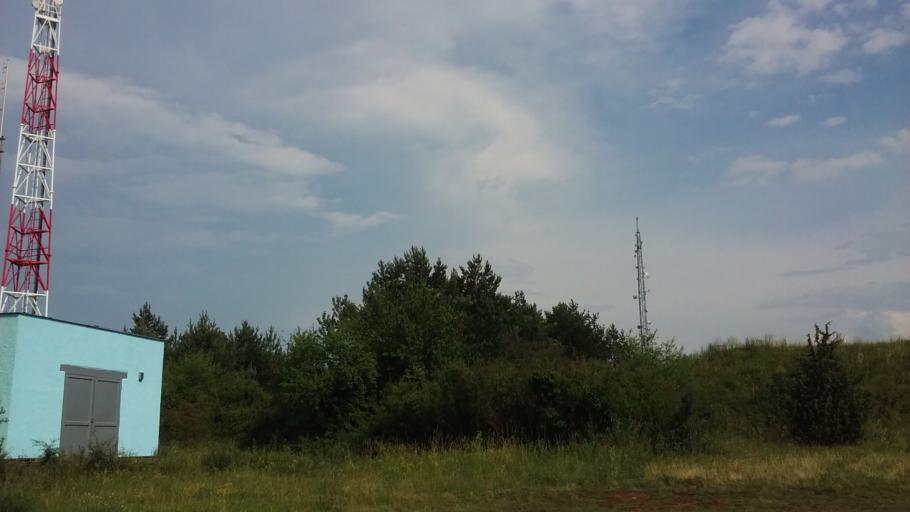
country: SK
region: Kosicky
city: Moldava nad Bodvou
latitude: 48.6157
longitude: 20.9830
